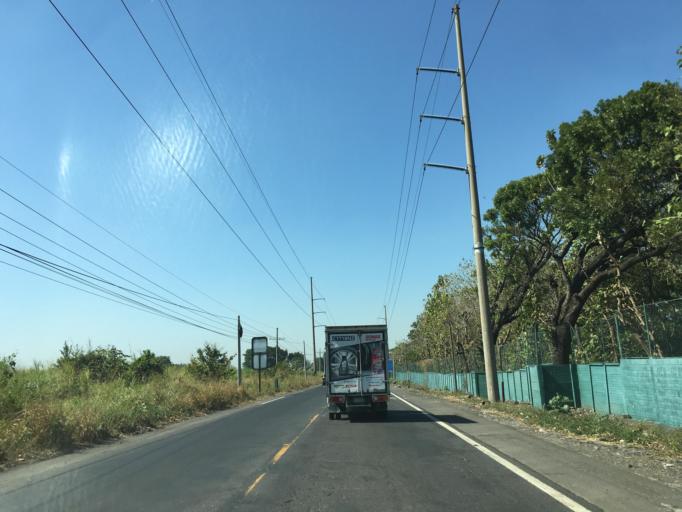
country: GT
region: Escuintla
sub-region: Municipio de Escuintla
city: Escuintla
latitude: 14.2540
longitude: -90.8024
